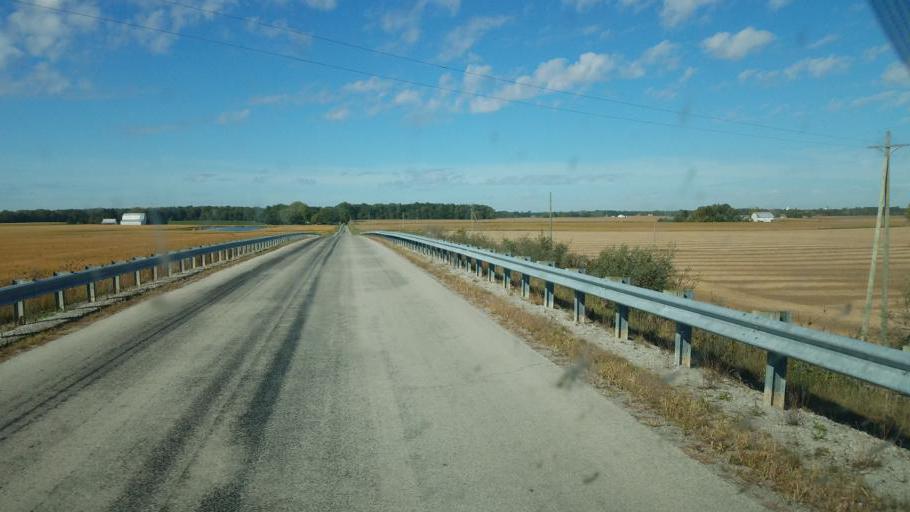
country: US
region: Ohio
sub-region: Wyandot County
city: Upper Sandusky
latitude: 40.8037
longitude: -83.2368
